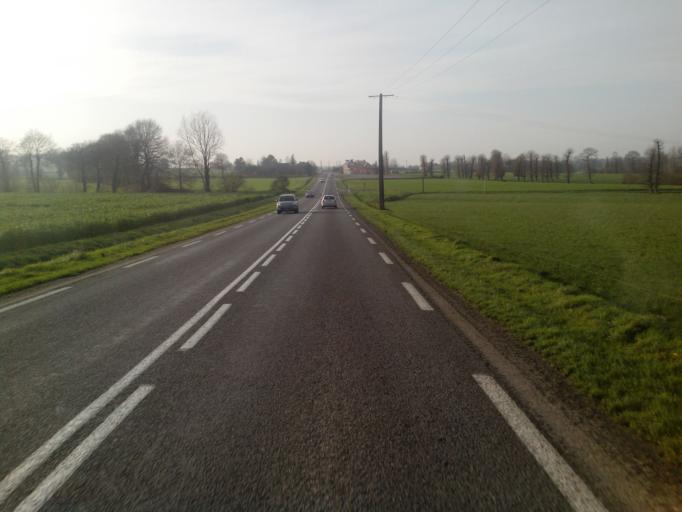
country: FR
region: Brittany
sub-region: Departement d'Ille-et-Vilaine
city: Boisgervilly
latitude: 48.1980
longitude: -2.0954
